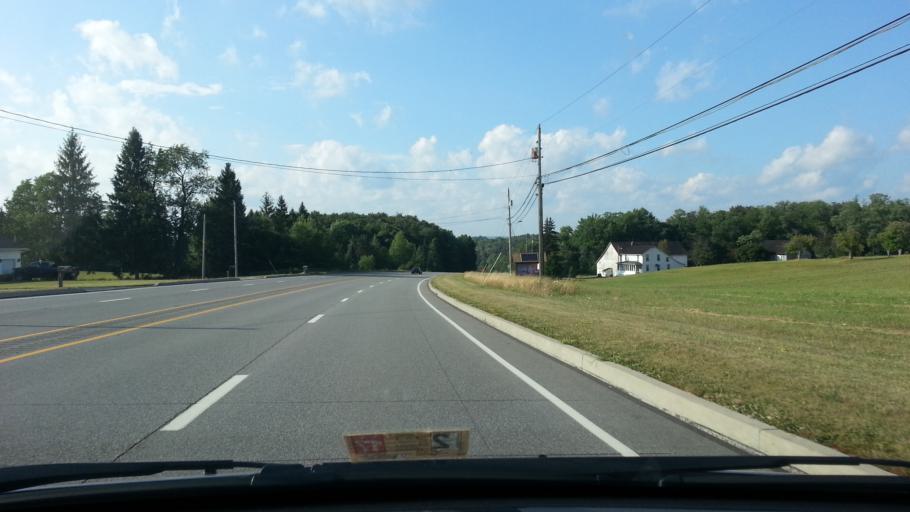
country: US
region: Pennsylvania
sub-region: Elk County
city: Saint Marys
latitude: 41.3779
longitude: -78.5588
